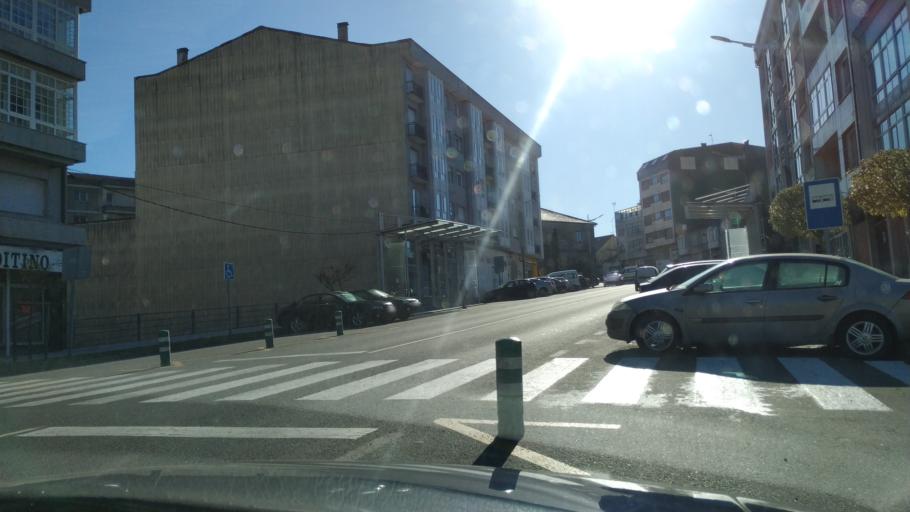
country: ES
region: Galicia
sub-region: Provincia de Pontevedra
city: Silleda
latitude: 42.6984
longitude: -8.2490
